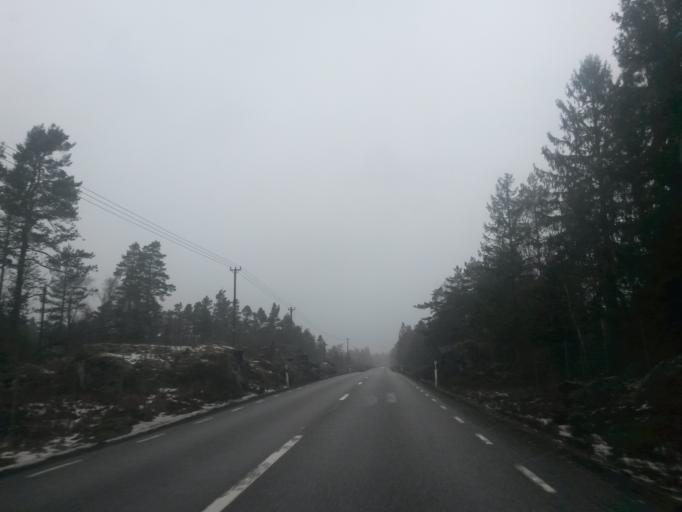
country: SE
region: Vaestra Goetaland
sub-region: Alingsas Kommun
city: Sollebrunn
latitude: 58.1939
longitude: 12.4314
